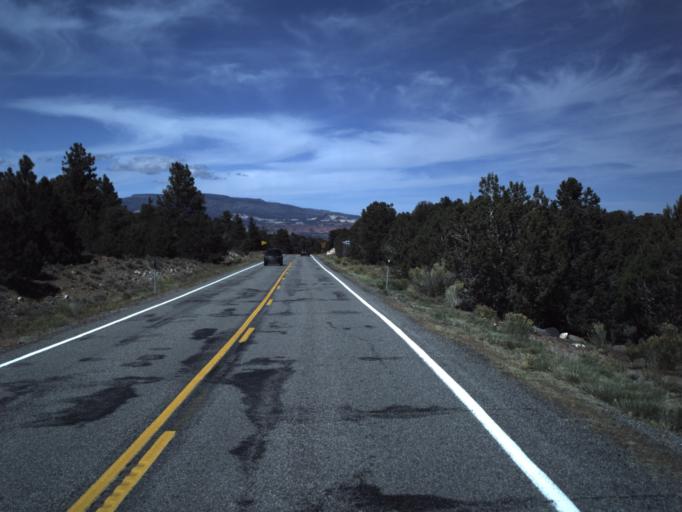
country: US
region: Utah
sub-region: Wayne County
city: Loa
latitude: 38.1941
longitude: -111.3506
